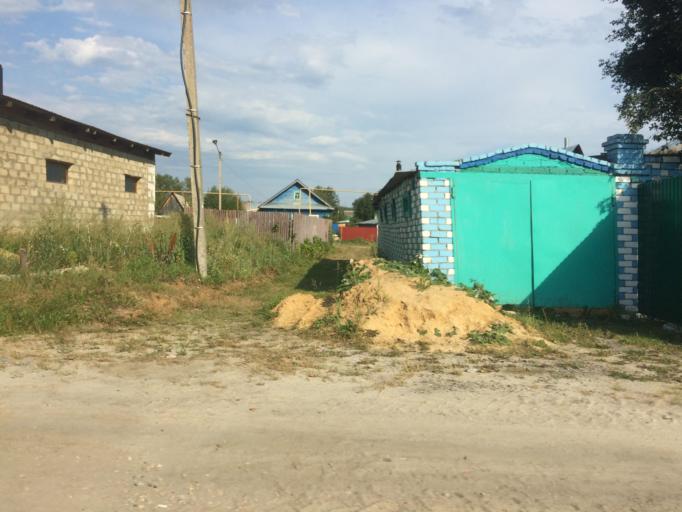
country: RU
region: Mariy-El
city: Yoshkar-Ola
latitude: 56.5478
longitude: 47.9826
